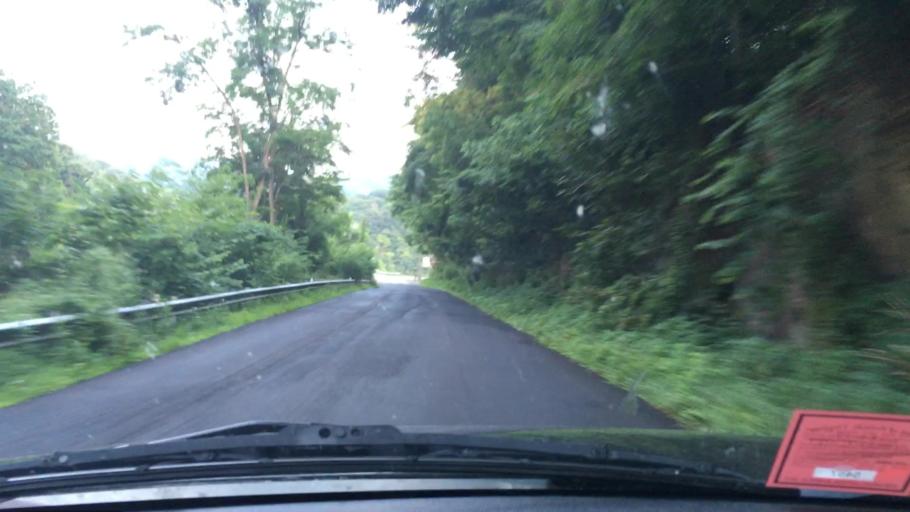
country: US
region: Virginia
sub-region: Pulaski County
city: Dublin
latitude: 37.0053
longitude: -80.6855
